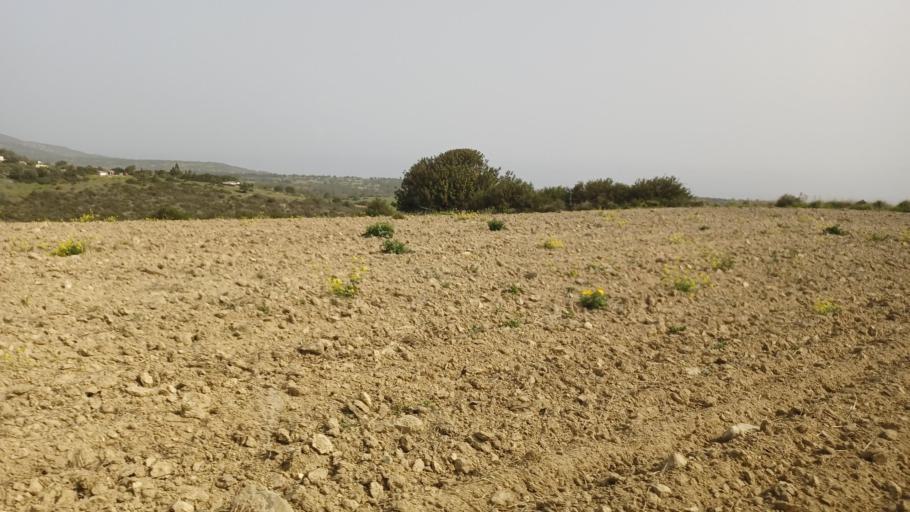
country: CY
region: Pafos
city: Polis
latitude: 35.0061
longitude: 32.3518
